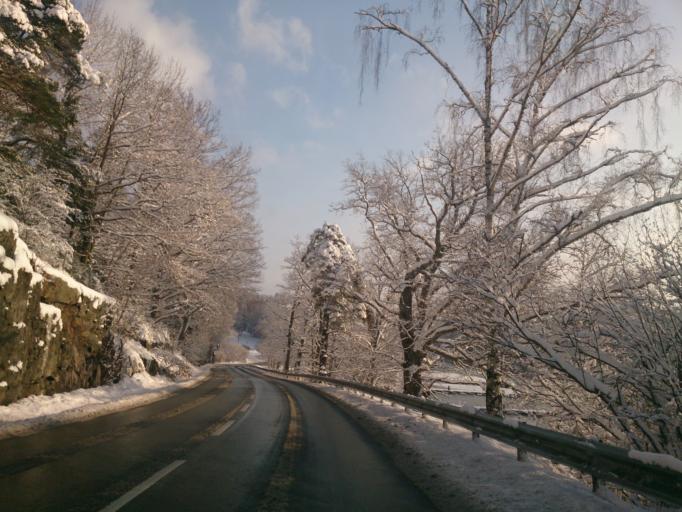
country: SE
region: Stockholm
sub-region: Varmdo Kommun
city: Hemmesta
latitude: 59.2874
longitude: 18.5390
